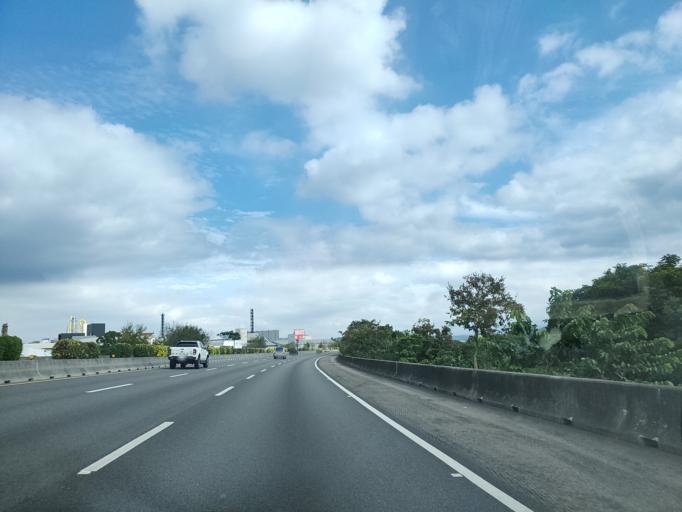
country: TW
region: Taiwan
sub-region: Miaoli
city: Miaoli
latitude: 24.6709
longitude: 120.8887
